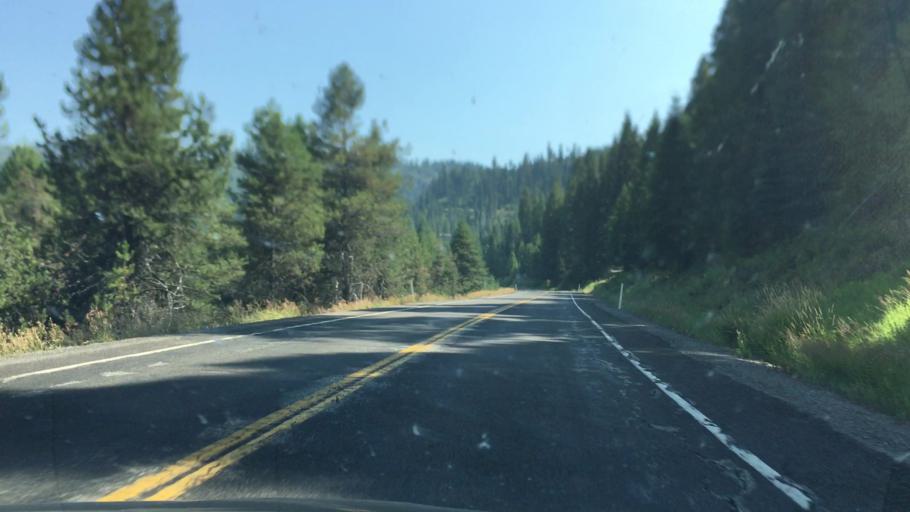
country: US
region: Idaho
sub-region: Valley County
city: Cascade
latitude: 44.2774
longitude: -116.0777
